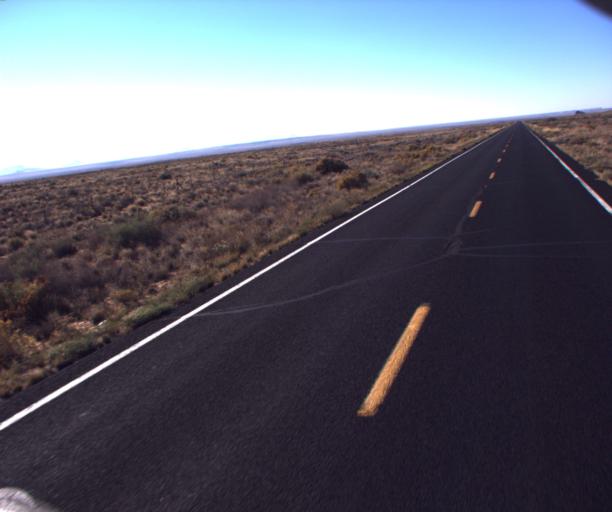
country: US
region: Arizona
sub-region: Navajo County
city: First Mesa
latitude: 35.7590
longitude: -110.5114
